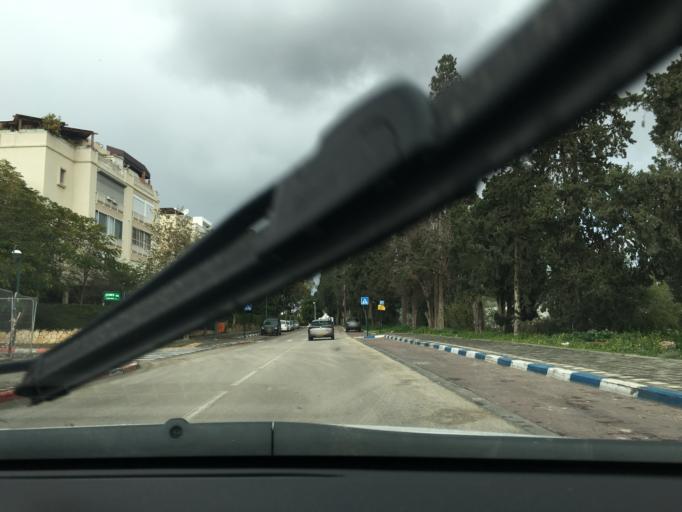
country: IL
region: Tel Aviv
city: Ramat HaSharon
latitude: 32.1418
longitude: 34.8467
